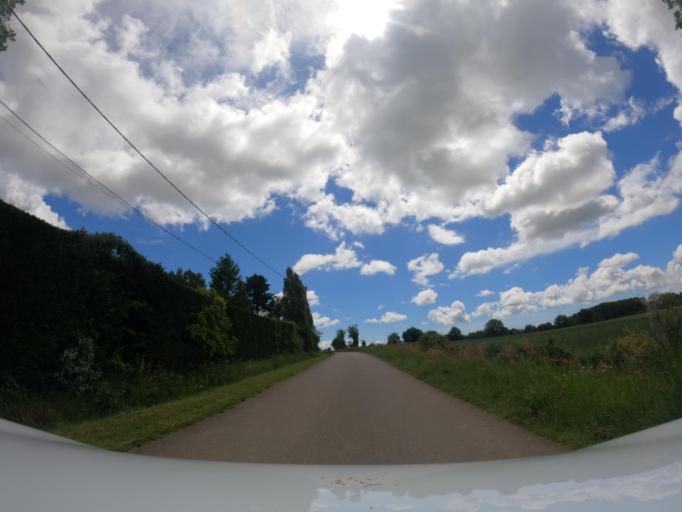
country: FR
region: Pays de la Loire
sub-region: Departement de la Vendee
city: Le Champ-Saint-Pere
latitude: 46.4837
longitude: -1.3587
